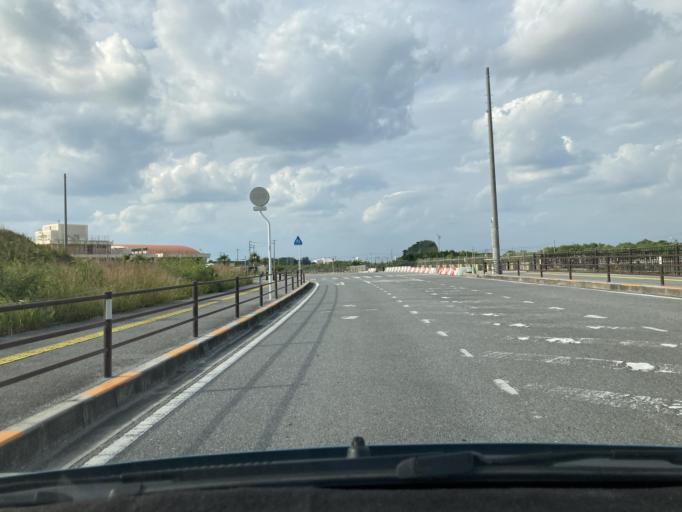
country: JP
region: Okinawa
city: Itoman
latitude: 26.1573
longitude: 127.6654
